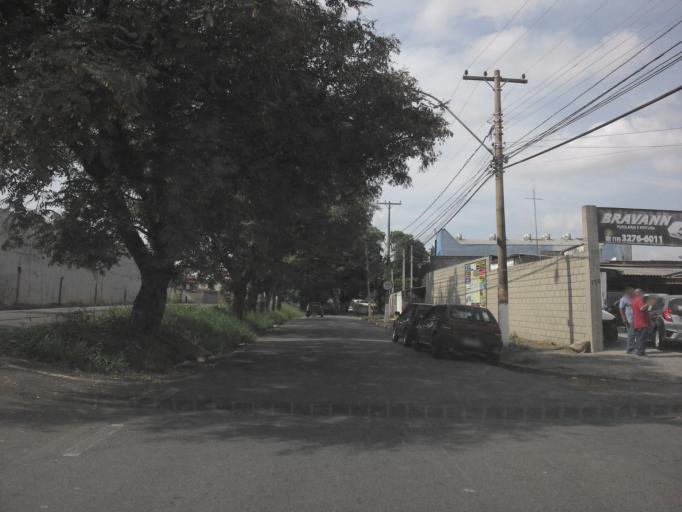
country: BR
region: Sao Paulo
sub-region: Campinas
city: Campinas
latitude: -22.9283
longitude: -47.0442
